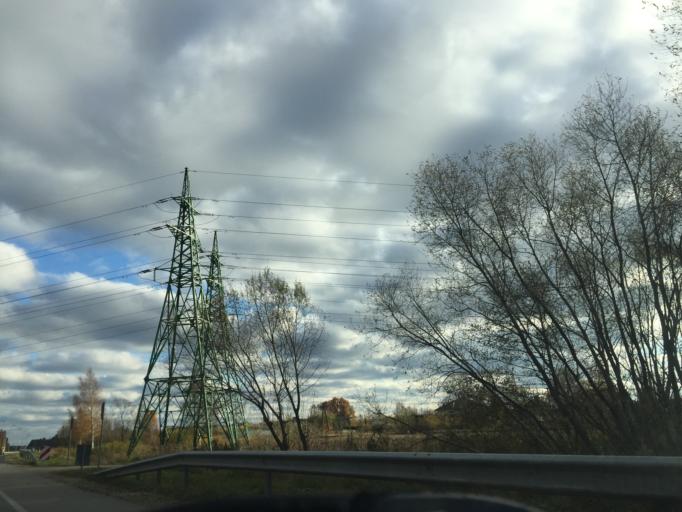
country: LV
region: Liepaja
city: Vec-Liepaja
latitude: 56.5393
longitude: 21.0804
